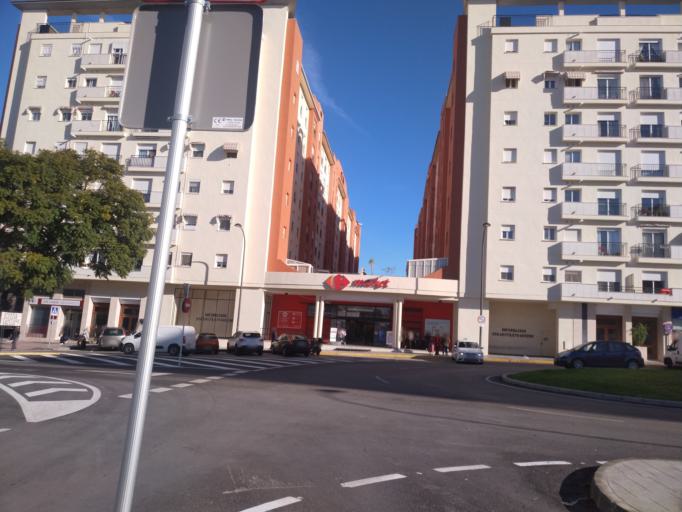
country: ES
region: Andalusia
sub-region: Provincia de Cadiz
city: San Fernando
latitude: 36.4697
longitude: -6.1994
